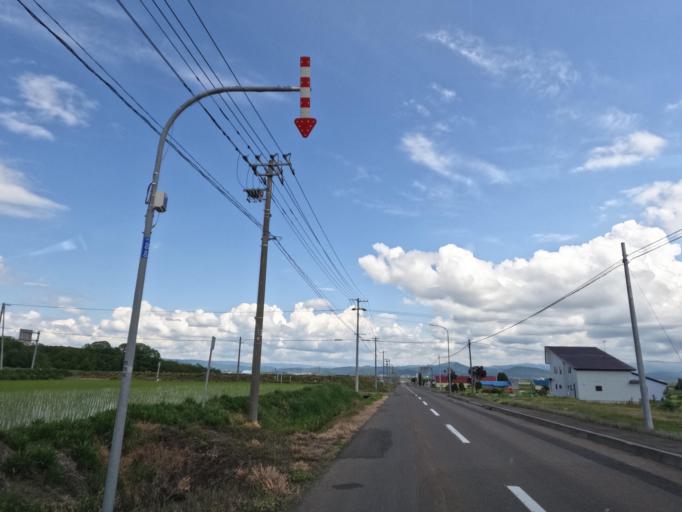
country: JP
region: Hokkaido
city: Takikawa
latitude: 43.5768
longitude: 141.8458
